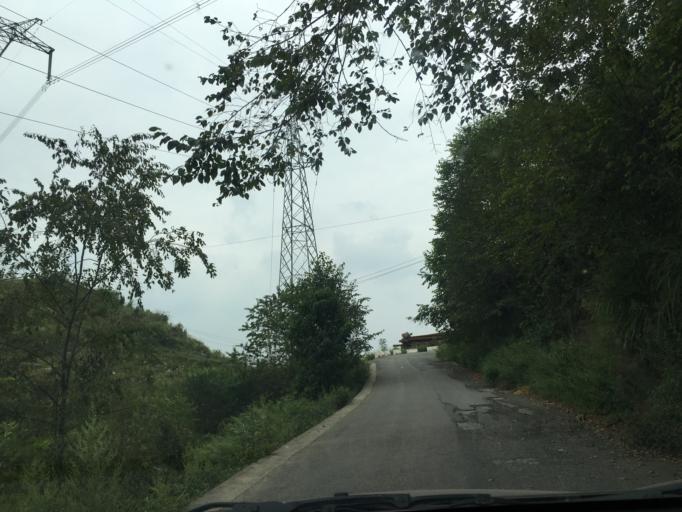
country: CN
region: Guangxi Zhuangzu Zizhiqu
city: Xinzhou
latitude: 25.5402
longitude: 105.5878
